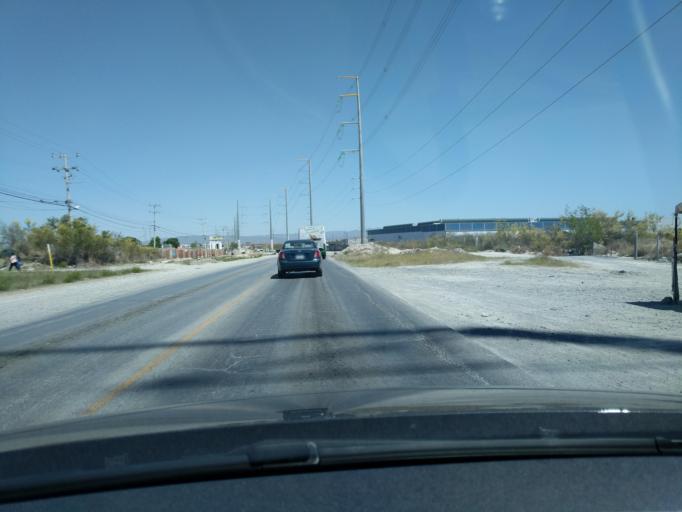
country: MX
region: Nuevo Leon
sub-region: Apodaca
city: Artemio Trevino
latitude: 25.8349
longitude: -100.1393
